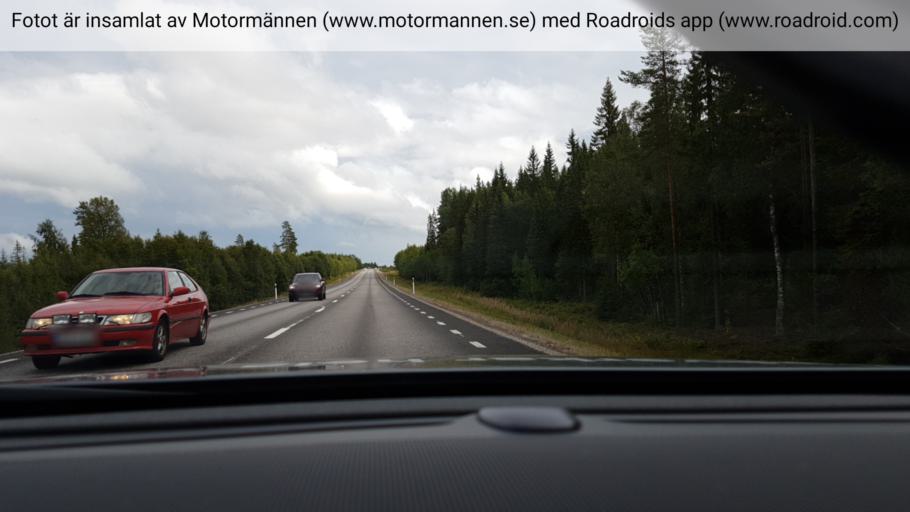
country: SE
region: Dalarna
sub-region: Rattviks Kommun
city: Raettvik
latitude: 60.8413
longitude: 15.2008
